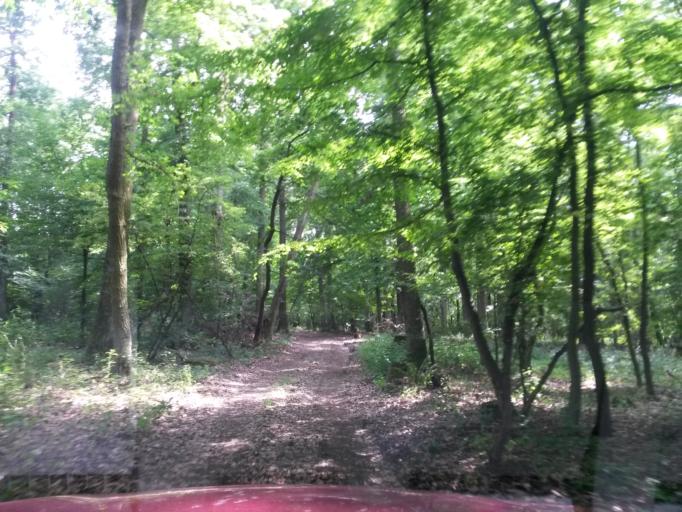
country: SK
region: Kosicky
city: Moldava nad Bodvou
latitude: 48.6358
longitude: 21.1029
